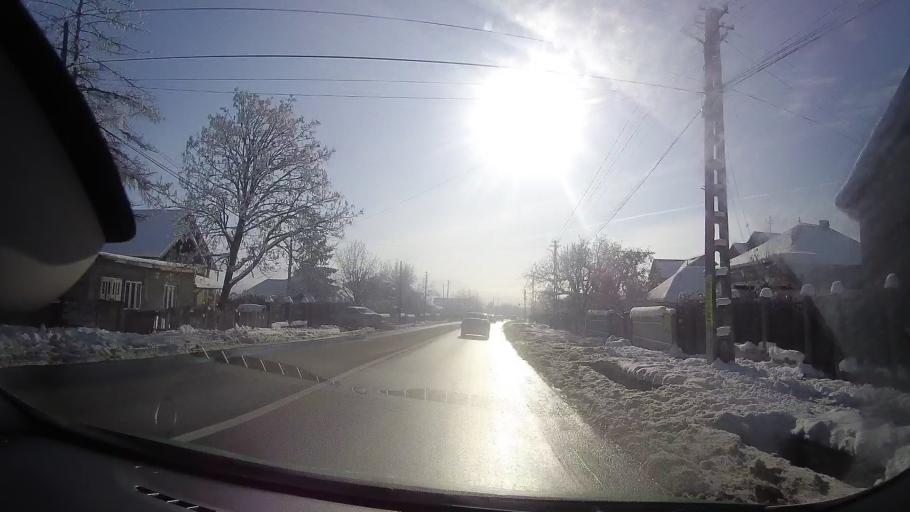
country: RO
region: Iasi
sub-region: Comuna Motca
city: Motca
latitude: 47.2455
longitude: 26.6086
